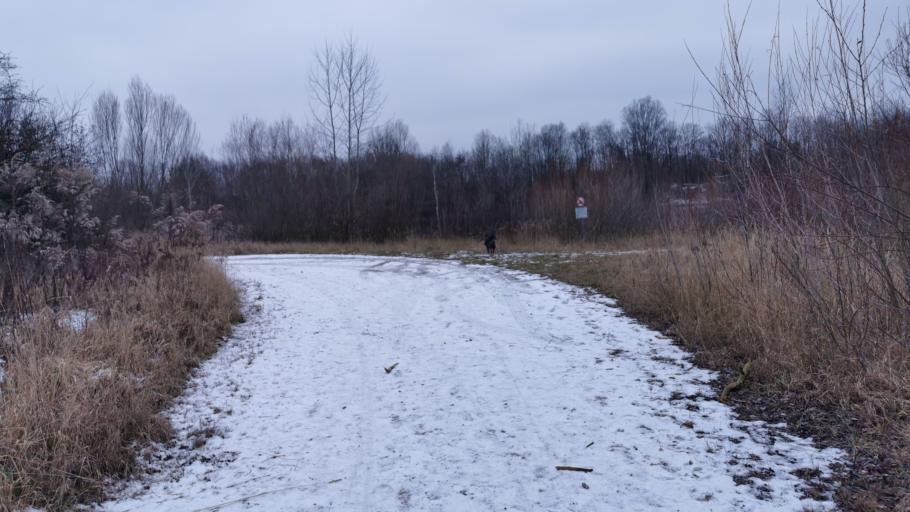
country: DE
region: Bavaria
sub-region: Upper Bavaria
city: Kirchheim bei Muenchen
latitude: 48.1940
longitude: 11.7622
